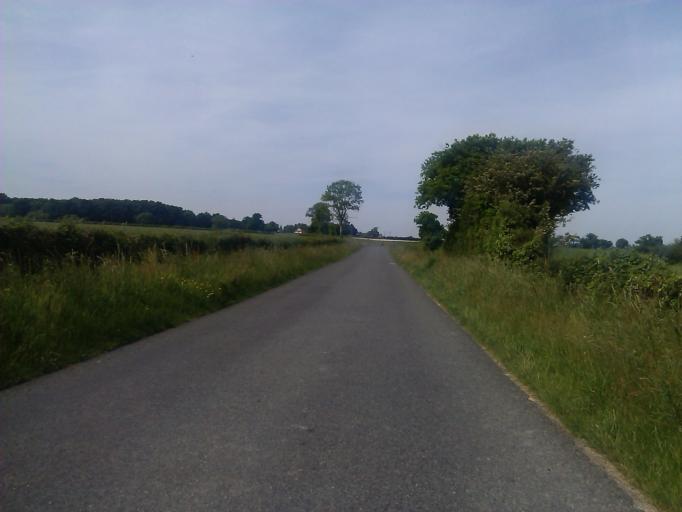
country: FR
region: Auvergne
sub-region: Departement de l'Allier
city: Vallon-en-Sully
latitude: 46.6061
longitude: 2.5241
